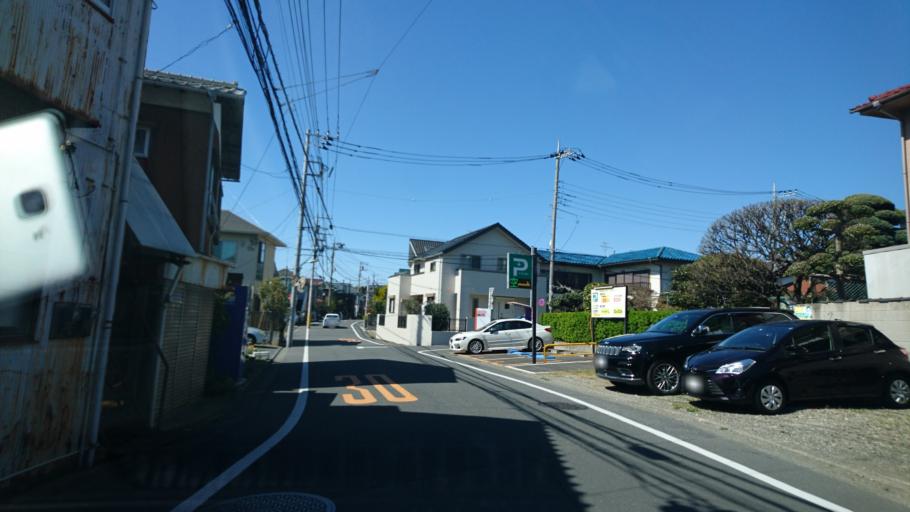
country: JP
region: Kanagawa
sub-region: Kawasaki-shi
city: Kawasaki
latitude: 35.5791
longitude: 139.7097
